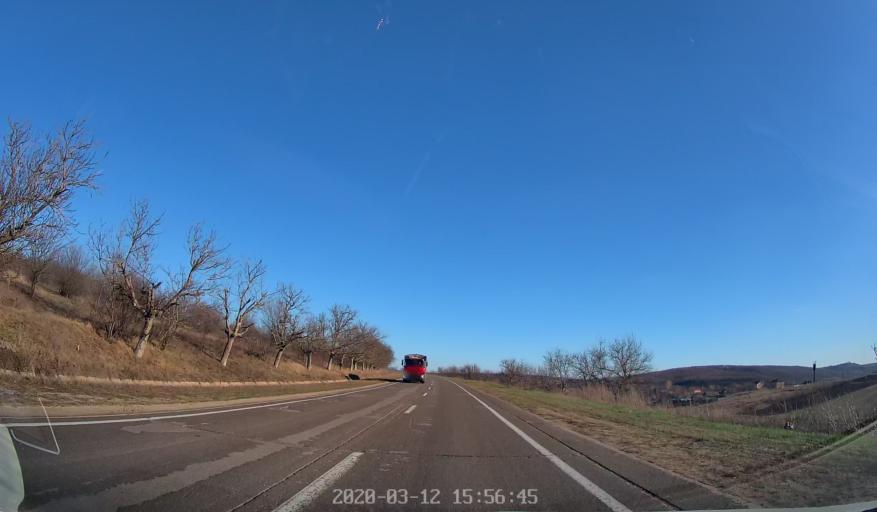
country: MD
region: Chisinau
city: Vadul lui Voda
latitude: 47.0595
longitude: 29.0365
